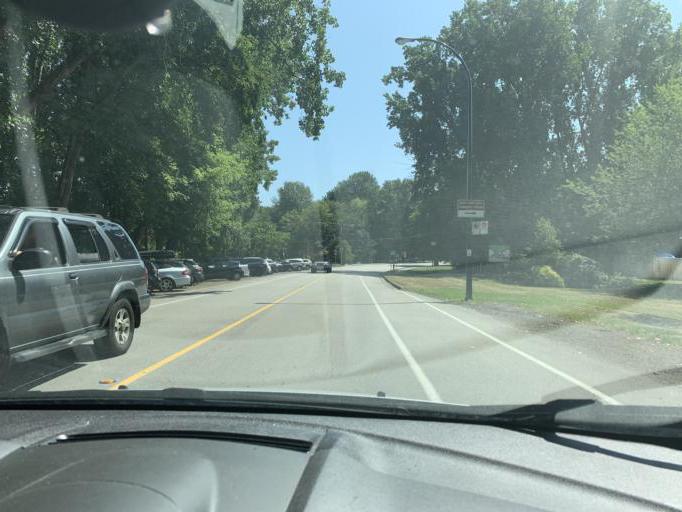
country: CA
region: British Columbia
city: West End
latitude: 49.2723
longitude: -123.2044
